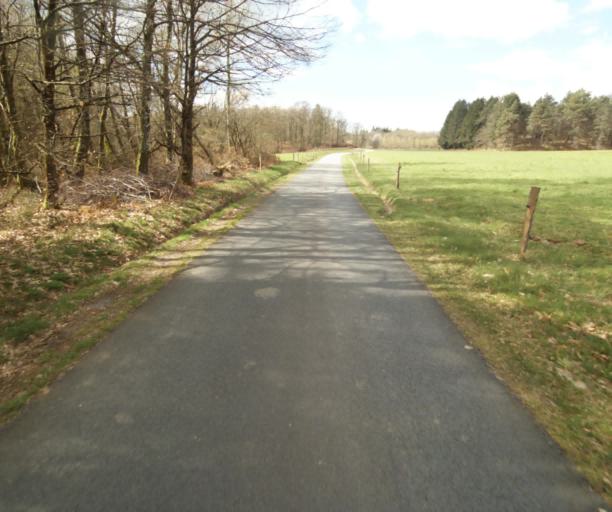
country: FR
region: Limousin
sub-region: Departement de la Correze
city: Correze
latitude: 45.2788
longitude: 1.9057
